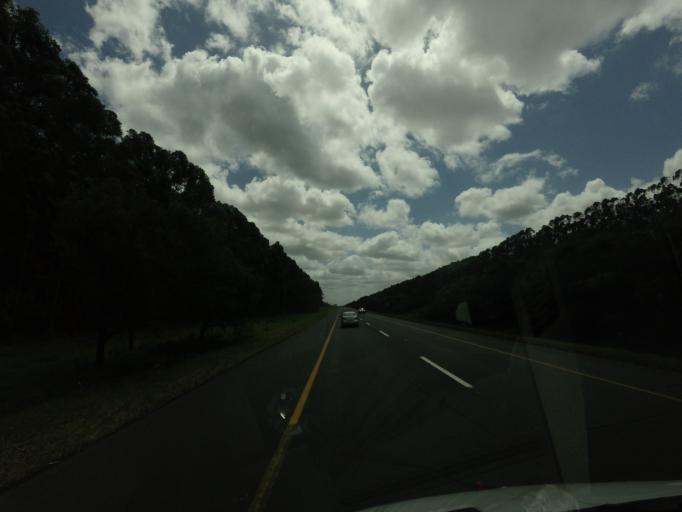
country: ZA
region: KwaZulu-Natal
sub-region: uThungulu District Municipality
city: KwaMbonambi
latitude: -28.5376
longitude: 32.1299
